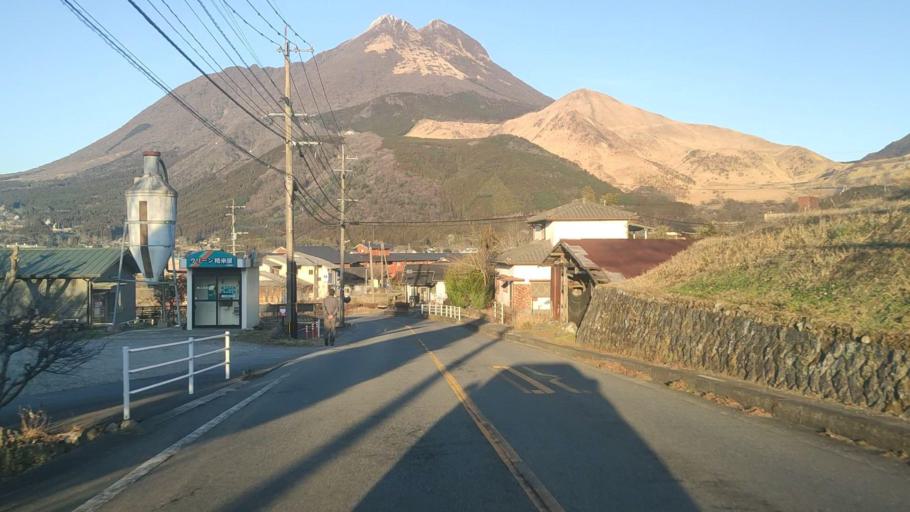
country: JP
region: Oita
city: Beppu
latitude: 33.2555
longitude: 131.3588
